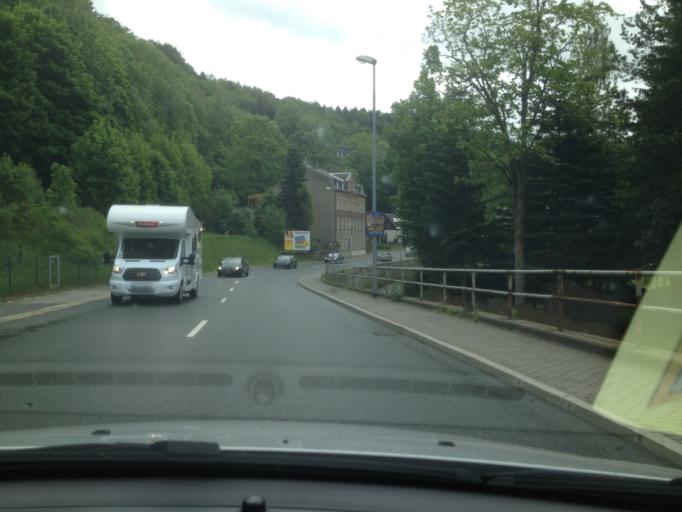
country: DE
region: Saxony
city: Annaberg-Buchholz
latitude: 50.5698
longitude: 12.9977
